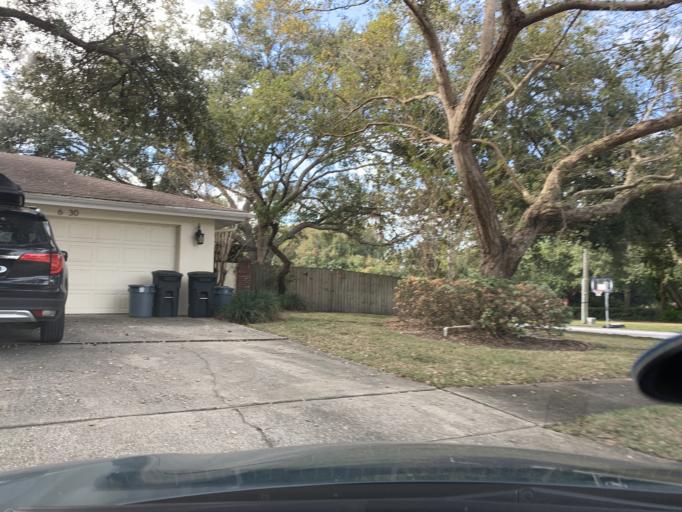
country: US
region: Florida
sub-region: Pinellas County
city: Kenneth City
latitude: 27.8280
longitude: -82.7403
